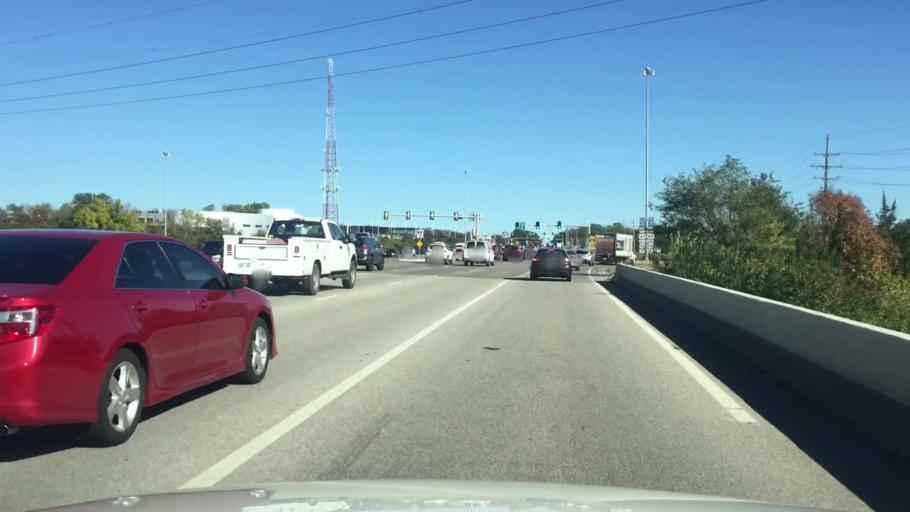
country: US
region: Kansas
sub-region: Johnson County
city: Merriam
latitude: 39.0147
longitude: -94.6962
